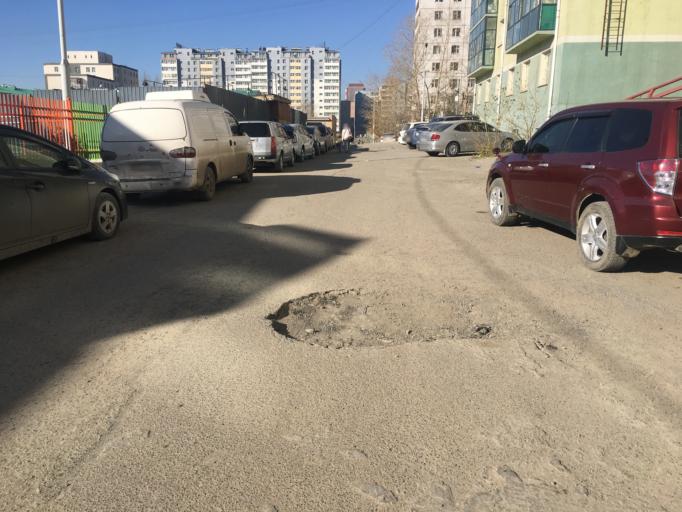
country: MN
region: Ulaanbaatar
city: Ulaanbaatar
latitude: 47.9212
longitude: 106.8873
